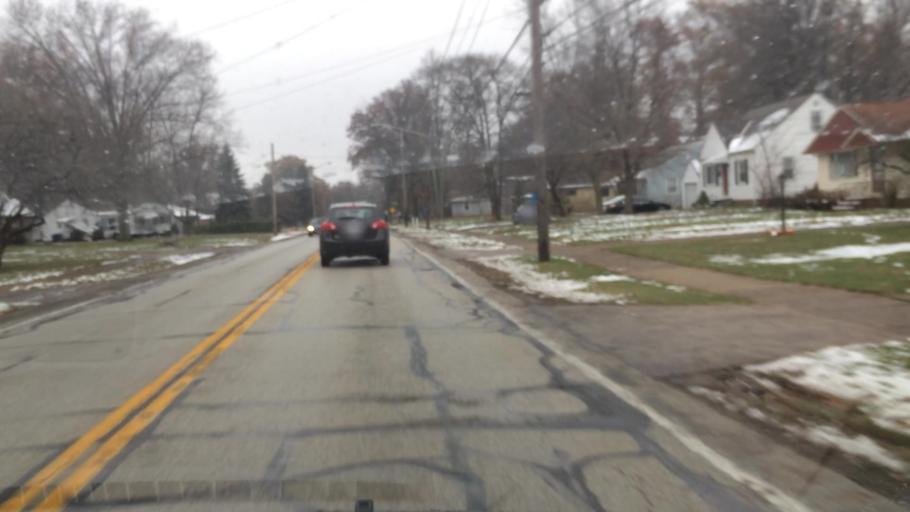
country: US
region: Ohio
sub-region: Cuyahoga County
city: North Olmsted
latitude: 41.4289
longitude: -81.8981
